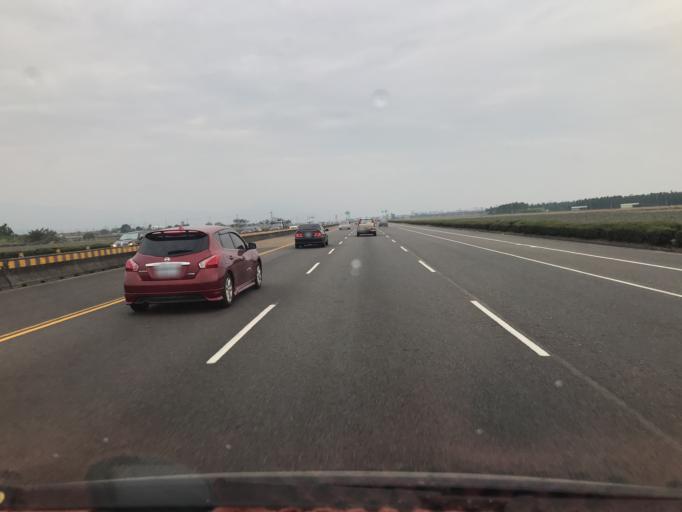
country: TW
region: Taiwan
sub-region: Pingtung
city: Pingtung
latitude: 22.4338
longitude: 120.5709
